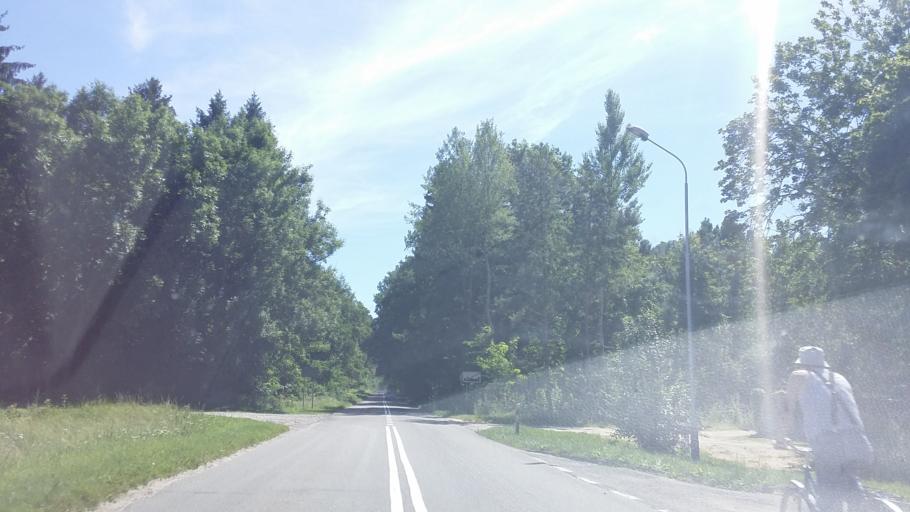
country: PL
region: West Pomeranian Voivodeship
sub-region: Powiat lobeski
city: Lobez
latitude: 53.6140
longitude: 15.6117
